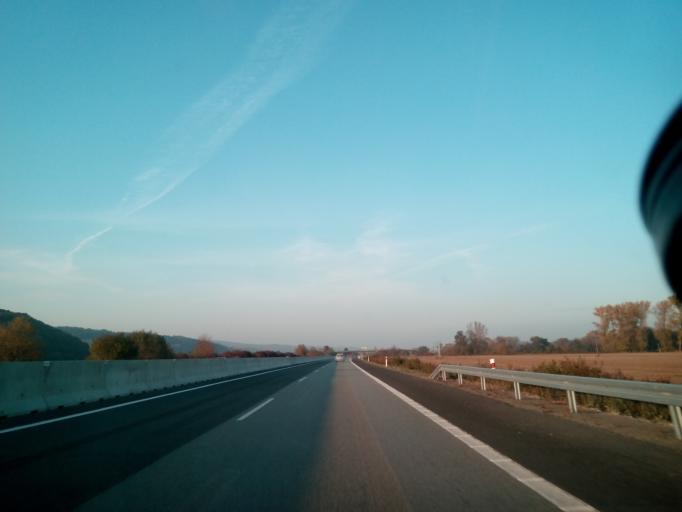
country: SK
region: Presovsky
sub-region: Okres Presov
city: Presov
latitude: 48.8881
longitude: 21.2494
